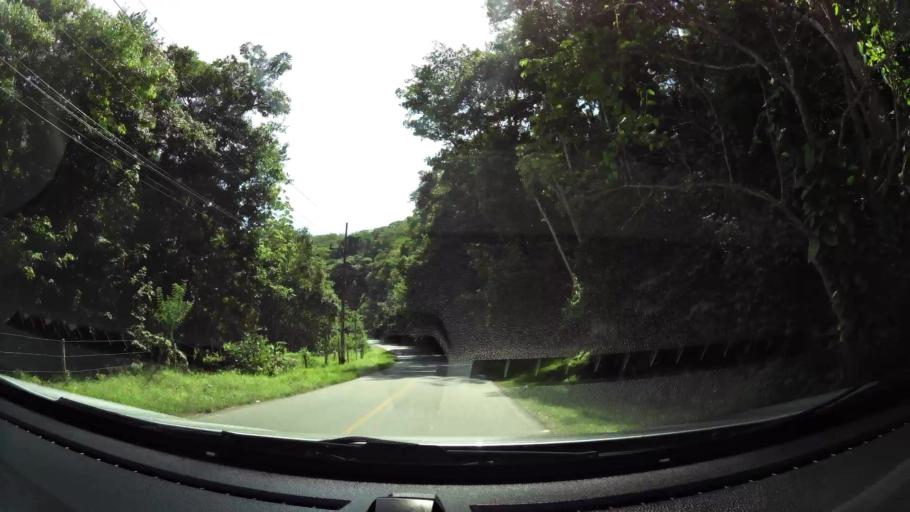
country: CR
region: San Jose
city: San Isidro
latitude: 9.2663
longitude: -83.8639
